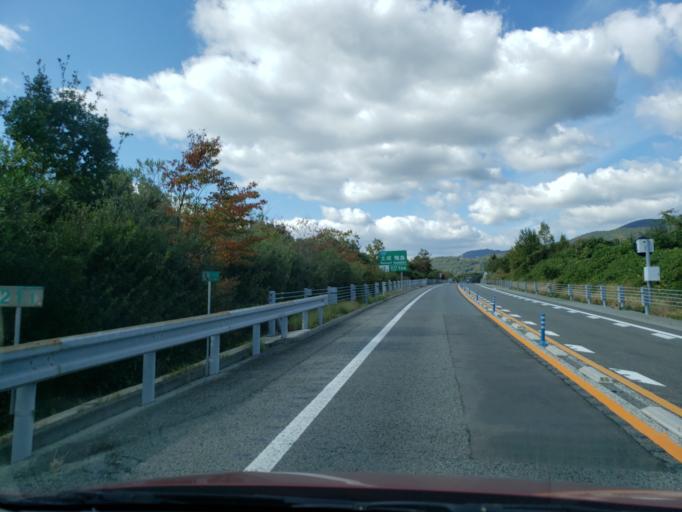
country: JP
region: Tokushima
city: Kamojimacho-jogejima
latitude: 34.1214
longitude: 134.3697
